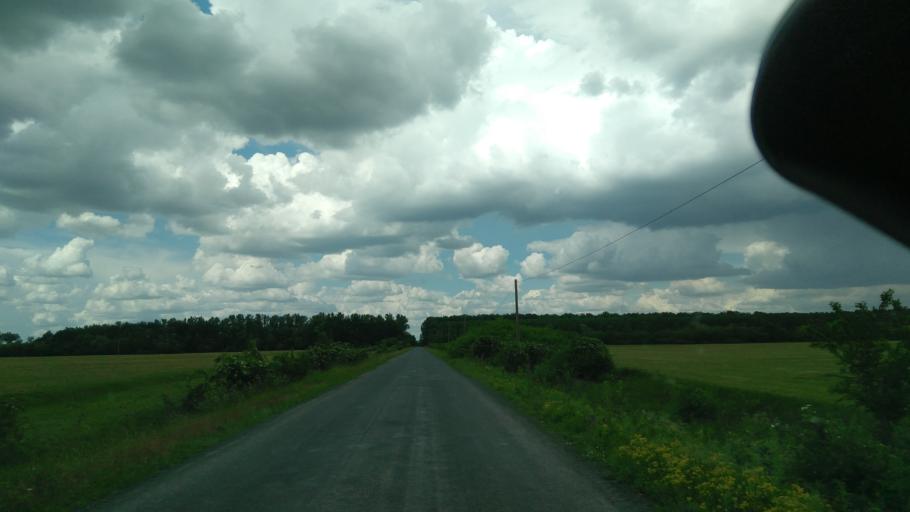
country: HU
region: Bekes
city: Szeghalom
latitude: 47.1124
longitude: 21.0879
